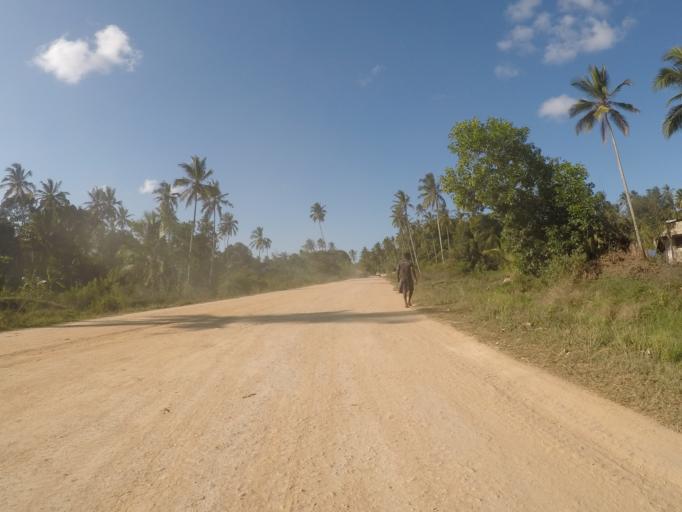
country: TZ
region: Zanzibar Central/South
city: Koani
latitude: -6.1739
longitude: 39.2844
